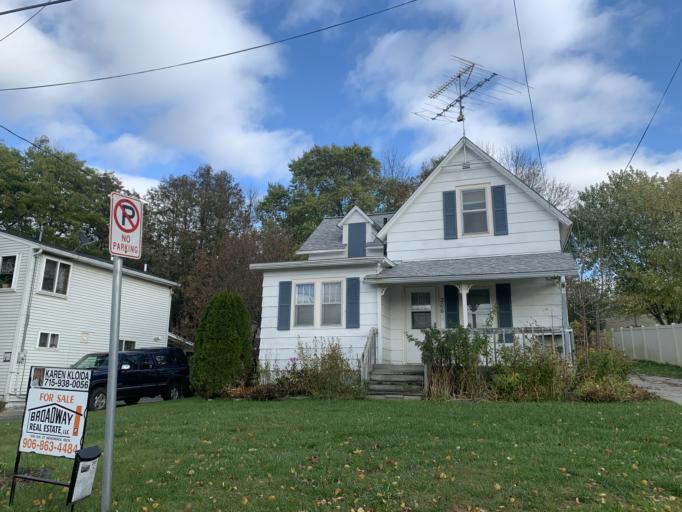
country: US
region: Michigan
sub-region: Menominee County
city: Menominee
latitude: 45.4159
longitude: -87.6061
